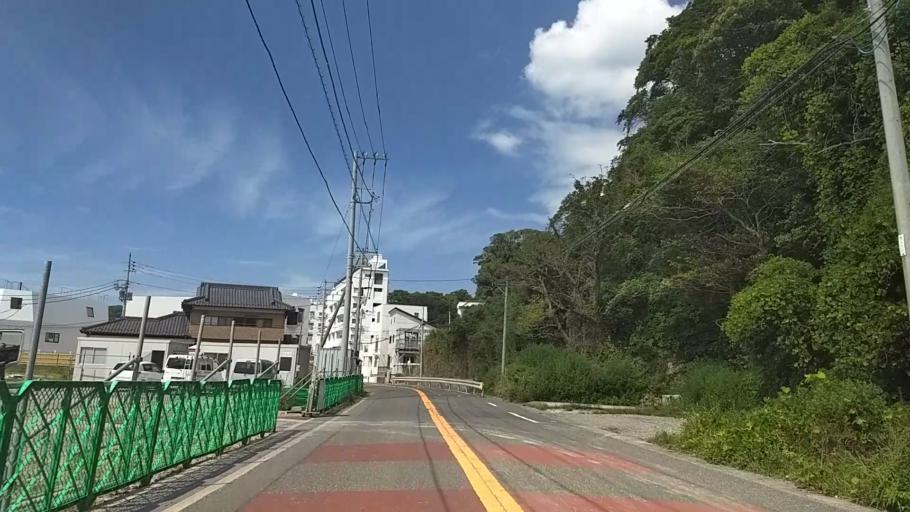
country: JP
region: Kanagawa
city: Hayama
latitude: 35.2250
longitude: 139.6036
